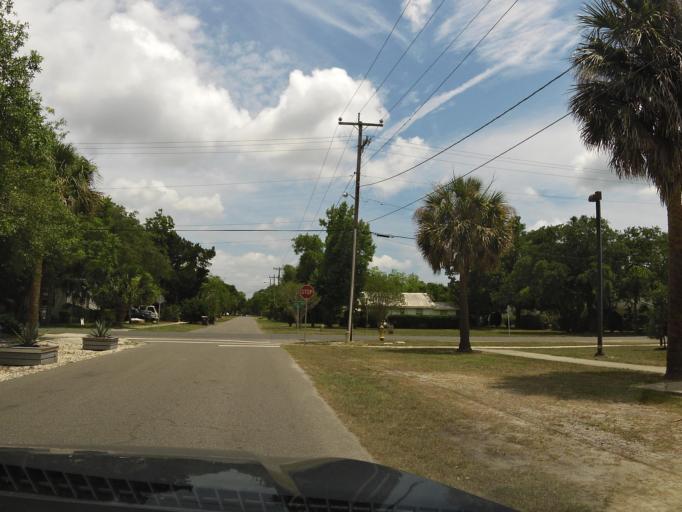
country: US
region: Florida
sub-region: Nassau County
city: Fernandina Beach
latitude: 30.6639
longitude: -81.4582
